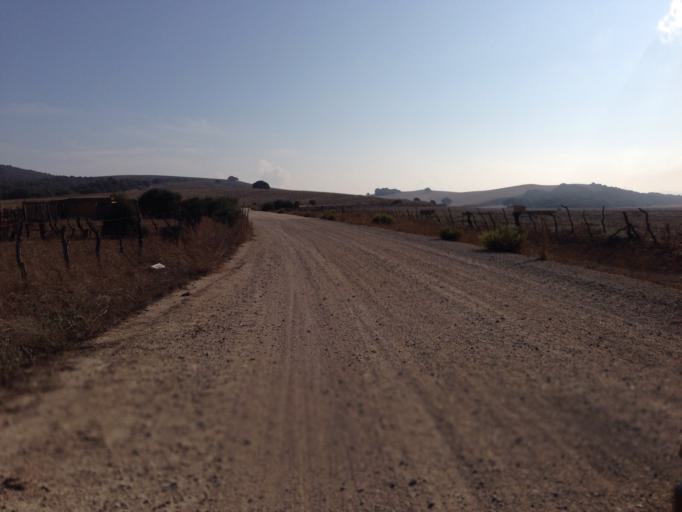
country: ES
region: Andalusia
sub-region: Provincia de Cadiz
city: Conil de la Frontera
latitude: 36.3212
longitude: -6.0141
